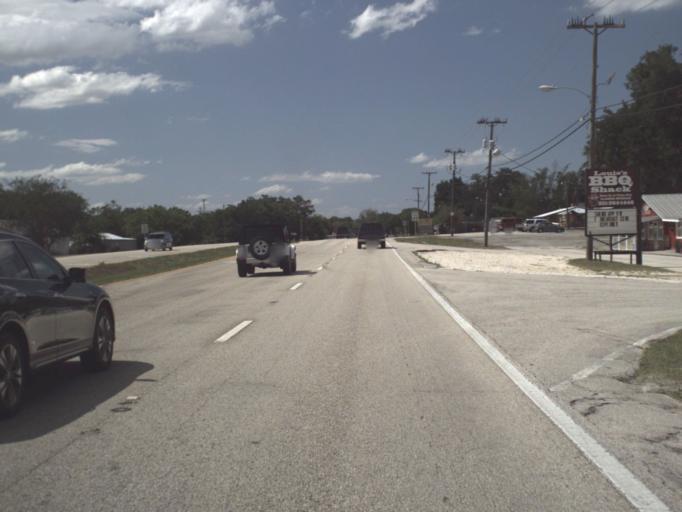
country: US
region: Florida
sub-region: Brevard County
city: Mims
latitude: 28.6562
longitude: -80.8412
